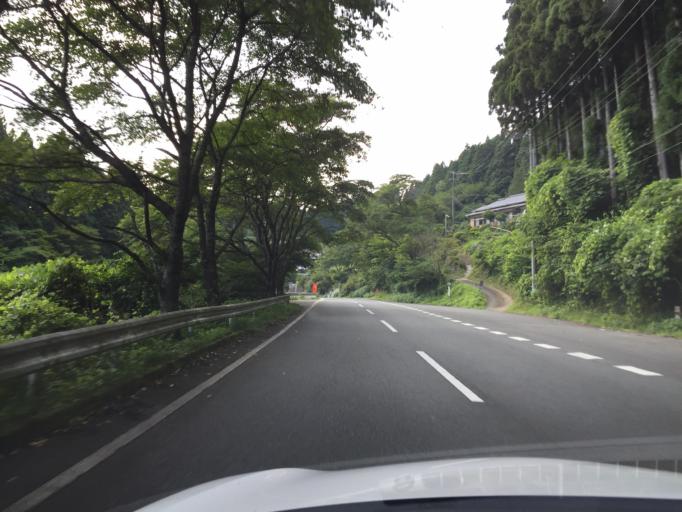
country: JP
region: Fukushima
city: Iwaki
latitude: 37.0086
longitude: 140.7186
